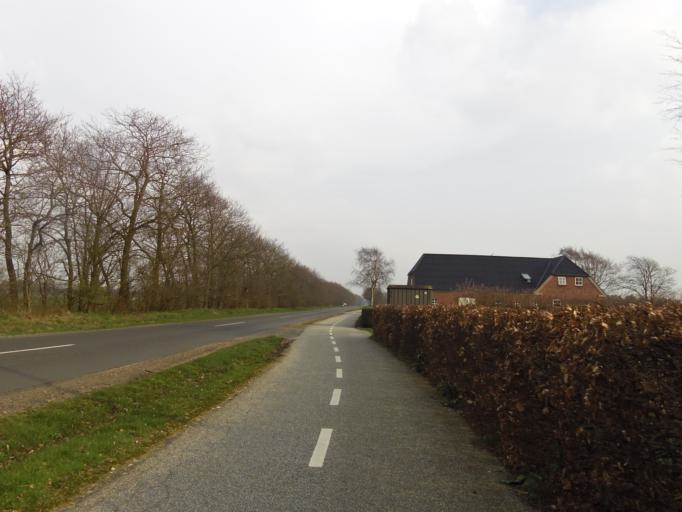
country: DK
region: South Denmark
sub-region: Esbjerg Kommune
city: Ribe
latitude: 55.3465
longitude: 8.7518
